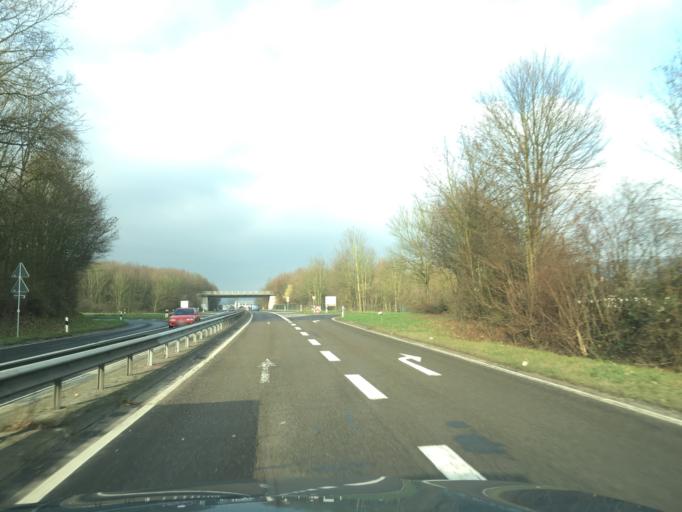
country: DE
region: Rheinland-Pfalz
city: Erpel
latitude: 50.5653
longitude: 7.2440
